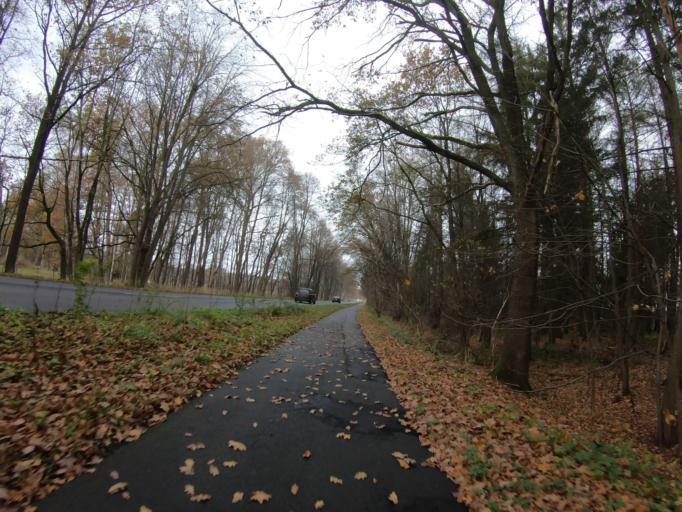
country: DE
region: Lower Saxony
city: Wagenhoff
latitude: 52.5456
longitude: 10.5168
